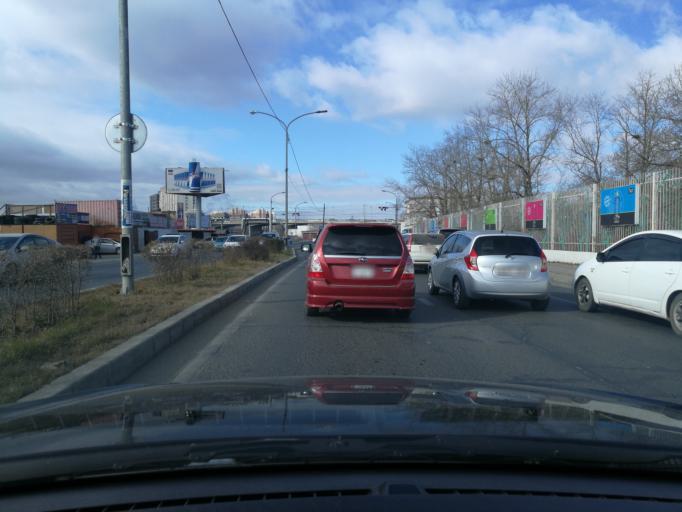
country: MN
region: Ulaanbaatar
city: Ulaanbaatar
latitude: 47.9081
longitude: 106.9167
